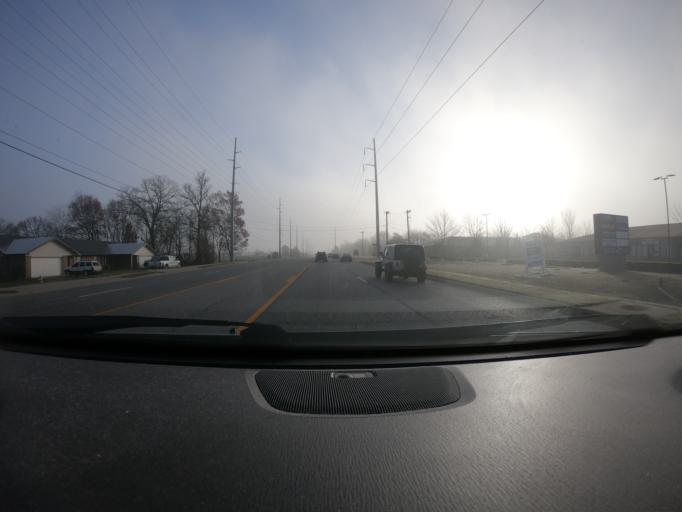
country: US
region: Arkansas
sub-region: Benton County
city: Bentonville
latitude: 36.3574
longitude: -94.2326
